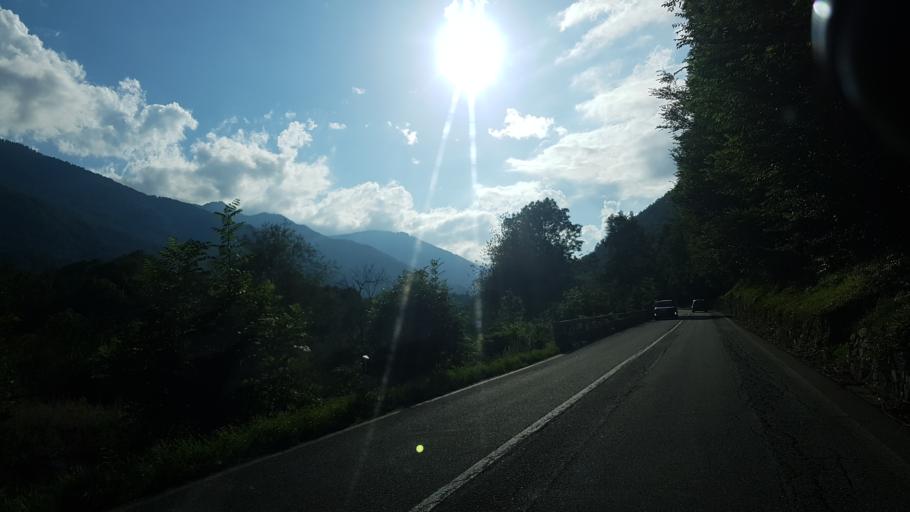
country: IT
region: Piedmont
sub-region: Provincia di Cuneo
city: Sampeyre
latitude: 44.5776
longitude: 7.2085
